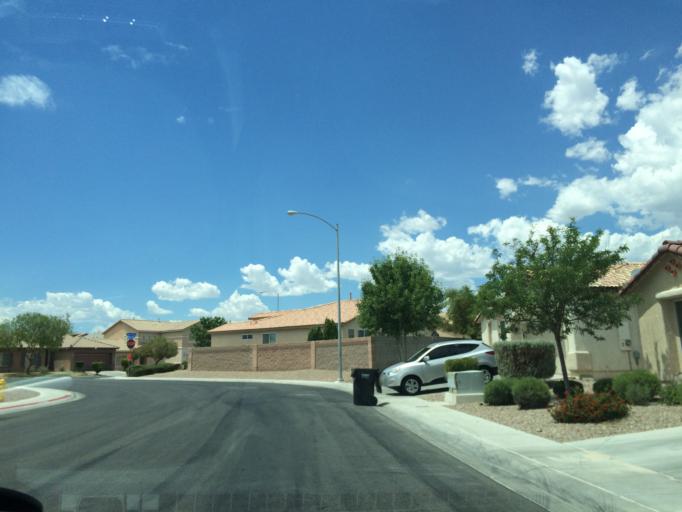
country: US
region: Nevada
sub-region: Clark County
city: North Las Vegas
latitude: 36.2595
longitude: -115.1838
